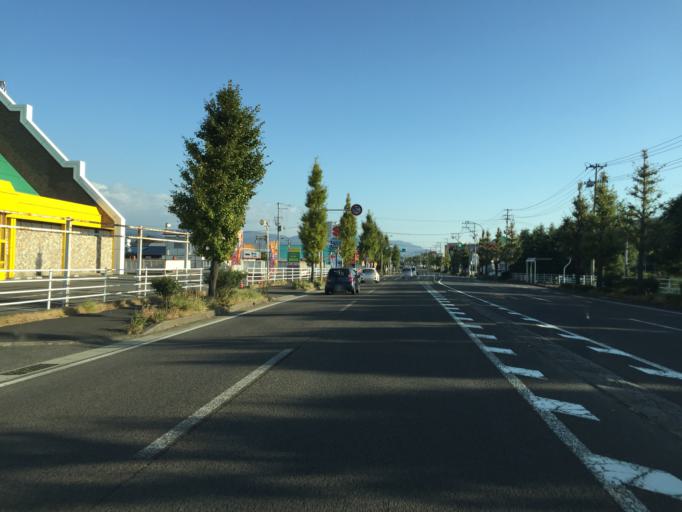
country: JP
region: Fukushima
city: Hobaramachi
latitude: 37.8110
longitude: 140.4982
